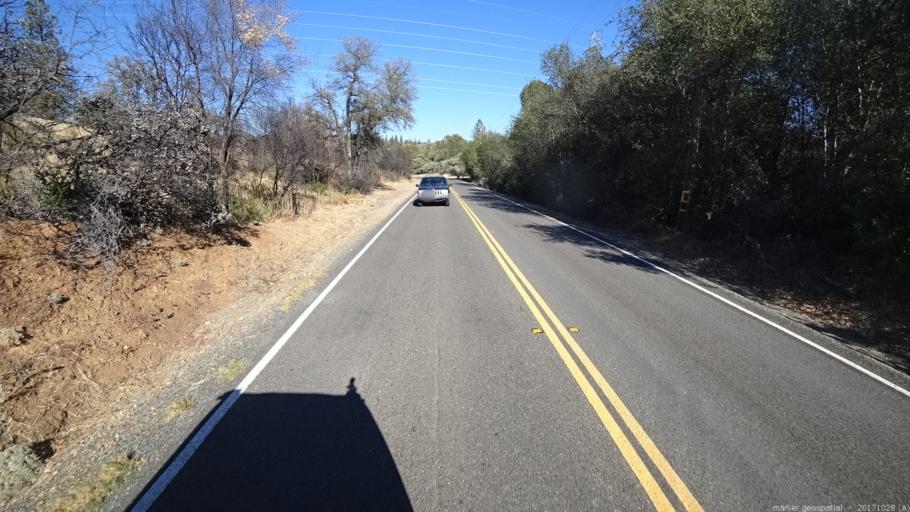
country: US
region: California
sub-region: Shasta County
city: Shasta
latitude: 40.6107
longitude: -122.4597
